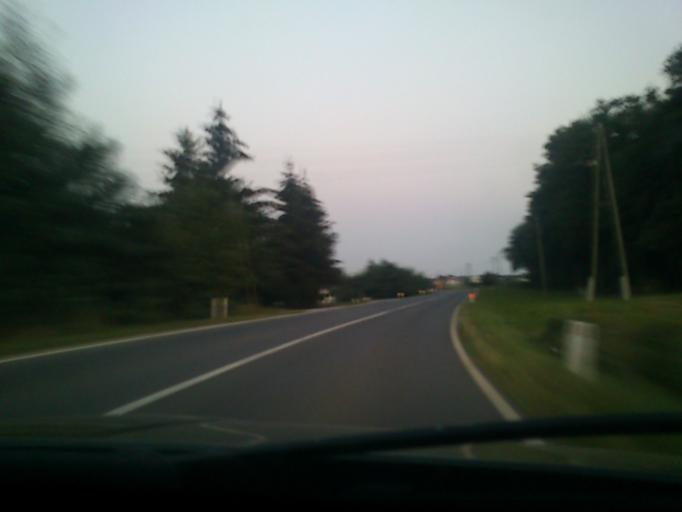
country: SI
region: Starse
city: Starse
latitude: 46.4711
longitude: 15.7557
